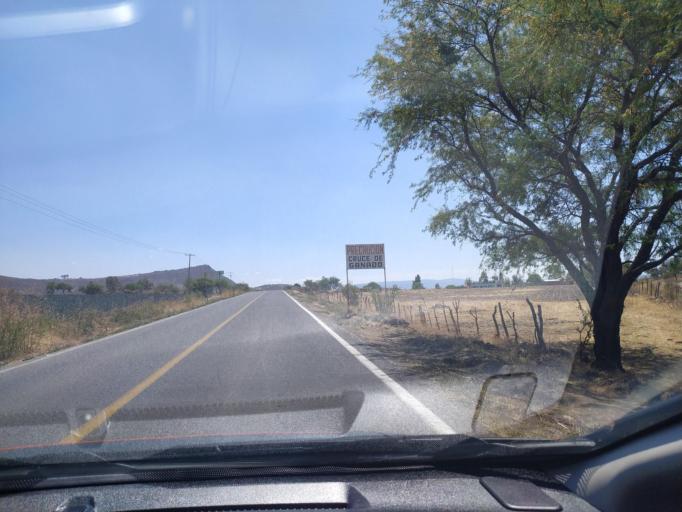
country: MX
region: Guanajuato
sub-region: San Francisco del Rincon
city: San Ignacio de Hidalgo
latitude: 20.8246
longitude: -101.8424
